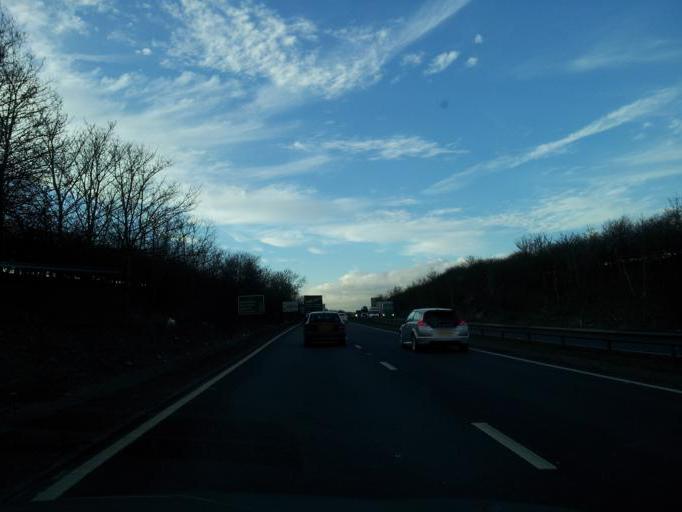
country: GB
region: England
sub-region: District of Rutland
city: Tinwell
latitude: 52.6486
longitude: -0.5077
